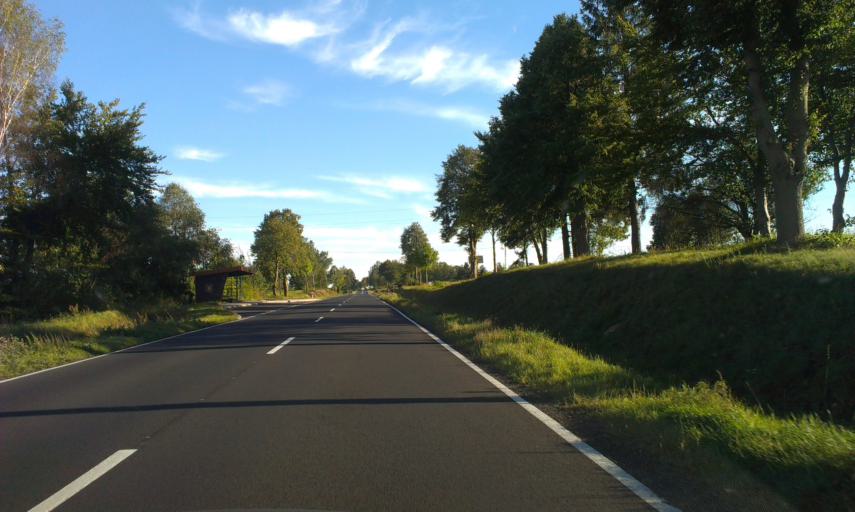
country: PL
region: West Pomeranian Voivodeship
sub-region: Powiat szczecinecki
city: Szczecinek
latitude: 53.7786
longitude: 16.6421
